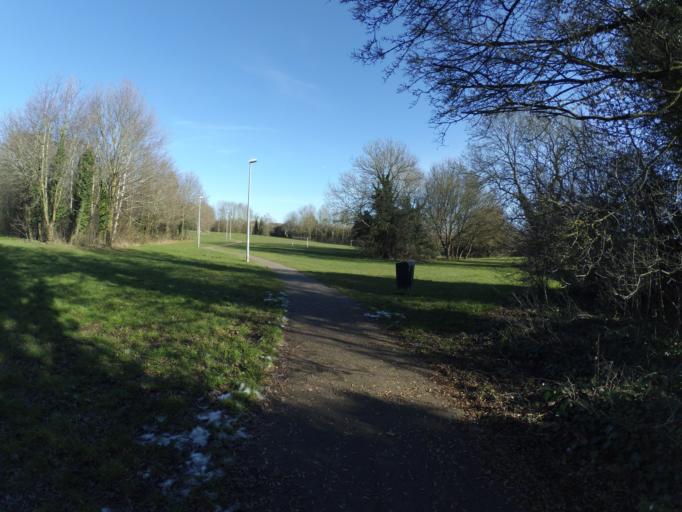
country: GB
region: England
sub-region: Warwickshire
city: Rugby
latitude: 52.3917
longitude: -1.2398
